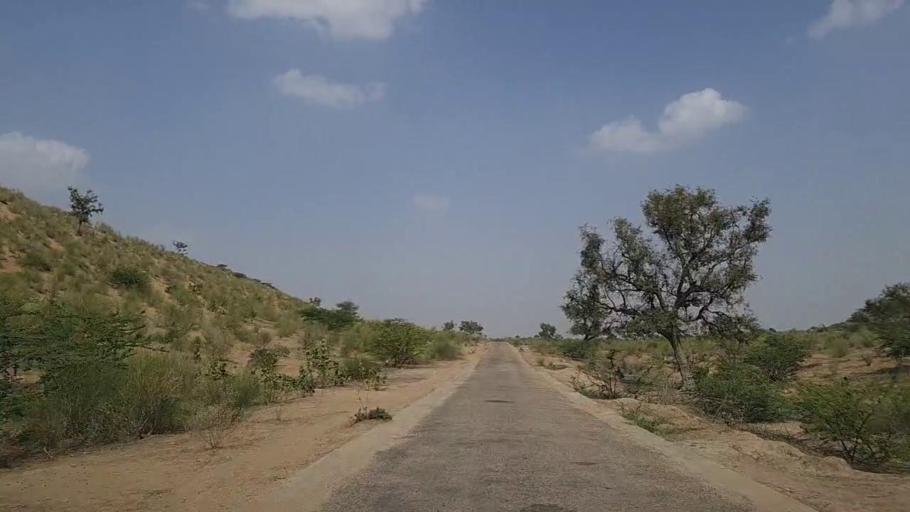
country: PK
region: Sindh
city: Islamkot
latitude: 24.7922
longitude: 70.1107
